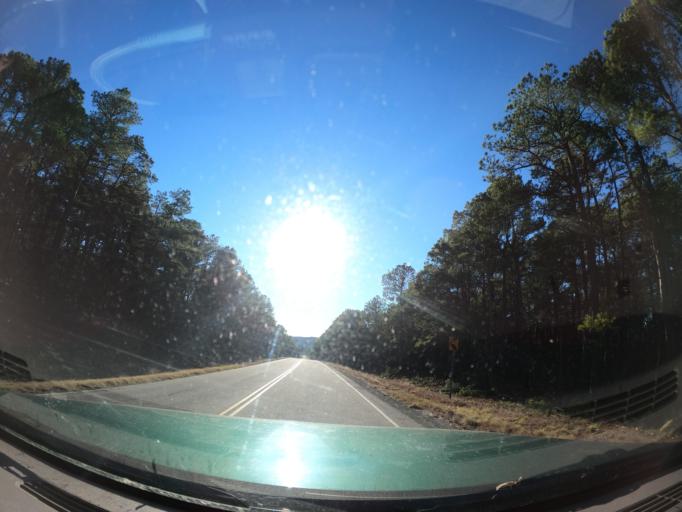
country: US
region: Oklahoma
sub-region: Latimer County
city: Wilburton
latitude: 35.0003
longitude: -95.3419
